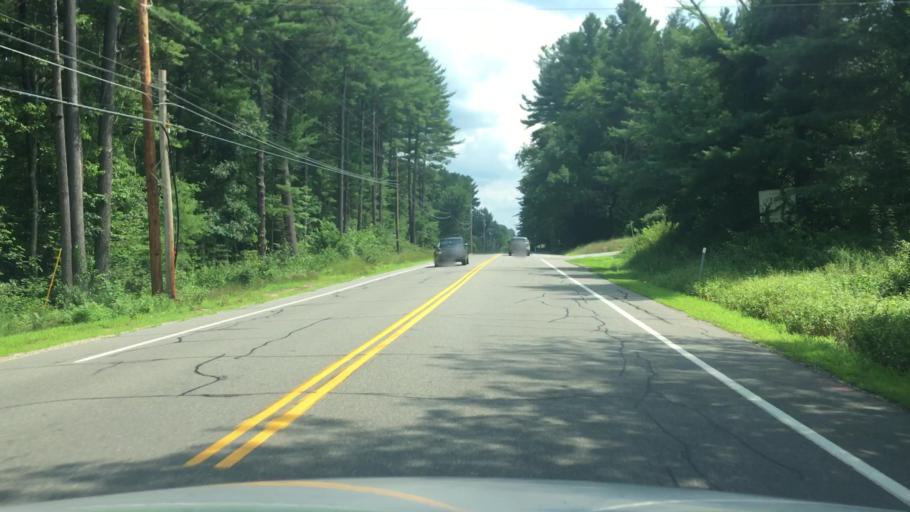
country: US
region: New Hampshire
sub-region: Rockingham County
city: Derry Village
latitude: 42.9418
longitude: -71.3466
